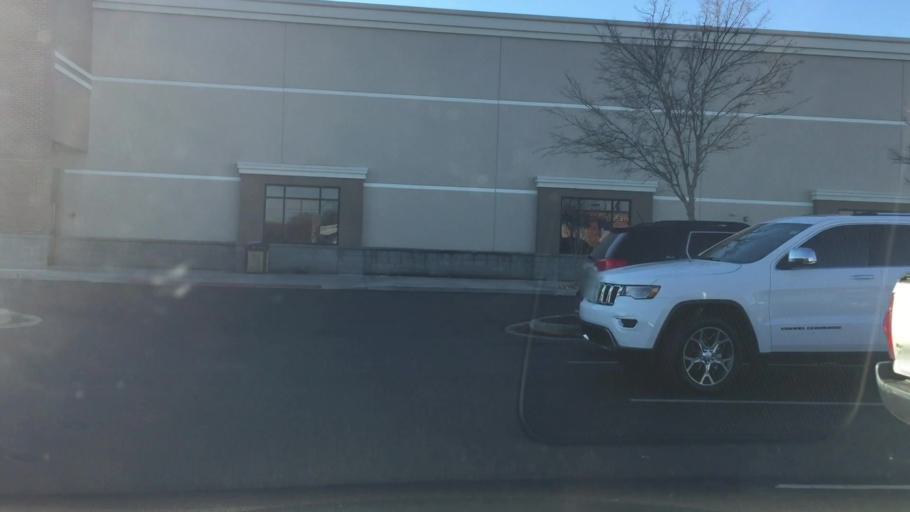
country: US
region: North Carolina
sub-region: Iredell County
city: Mooresville
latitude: 35.5932
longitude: -80.8648
